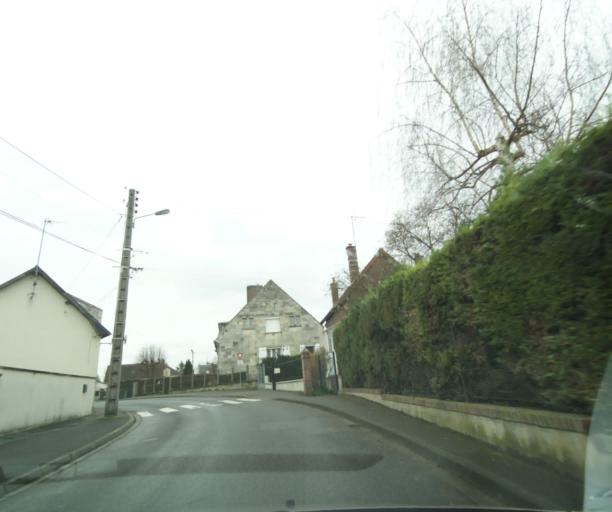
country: FR
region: Picardie
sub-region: Departement de l'Oise
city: Noyon
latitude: 49.5746
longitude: 3.0011
